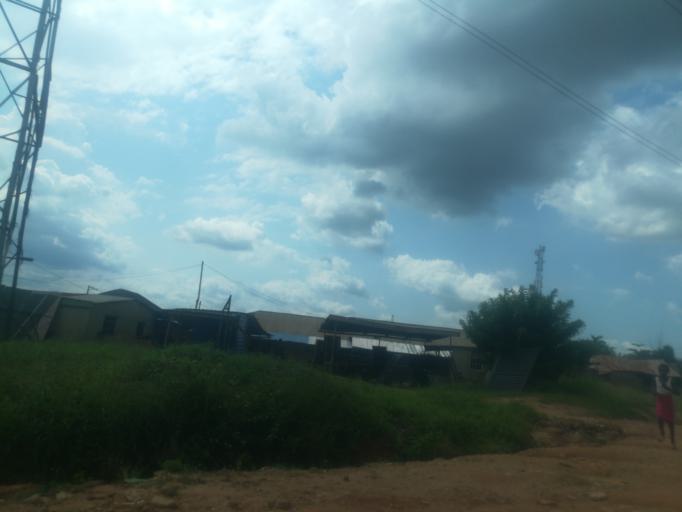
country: NG
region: Oyo
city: Ibadan
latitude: 7.4202
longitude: 3.8472
